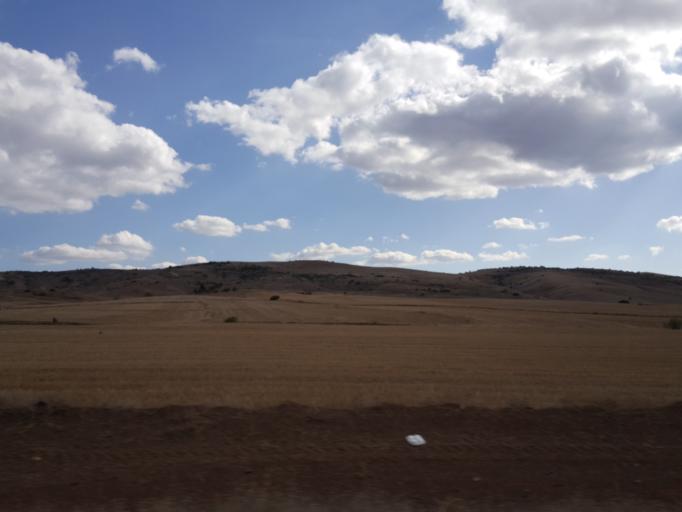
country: TR
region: Tokat
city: Sulusaray
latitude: 39.9865
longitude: 35.9600
